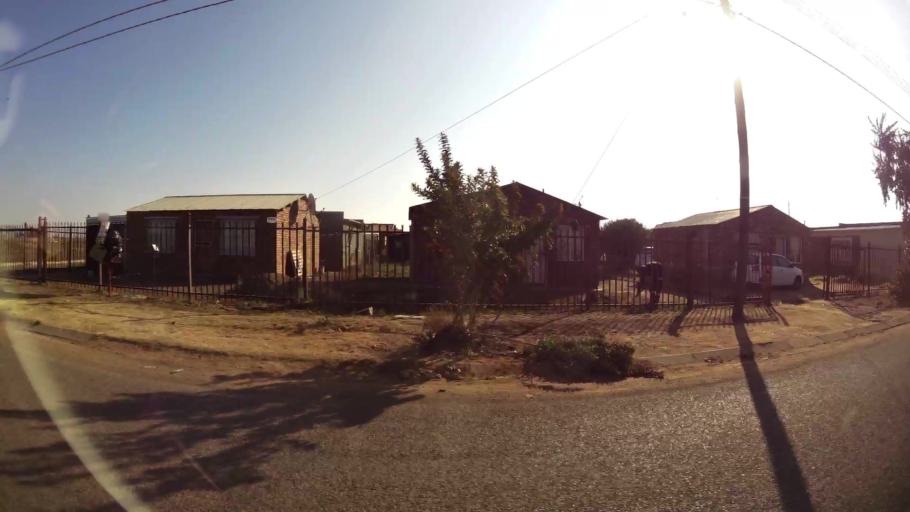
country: ZA
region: Orange Free State
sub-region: Mangaung Metropolitan Municipality
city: Bloemfontein
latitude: -29.2013
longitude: 26.2183
